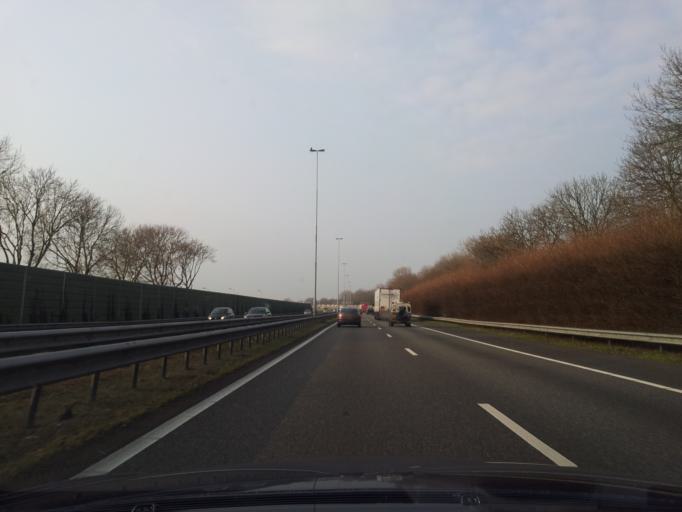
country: NL
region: North Brabant
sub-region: Gemeente Geertruidenberg
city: Geertruidenberg
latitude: 51.7347
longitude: 4.9066
